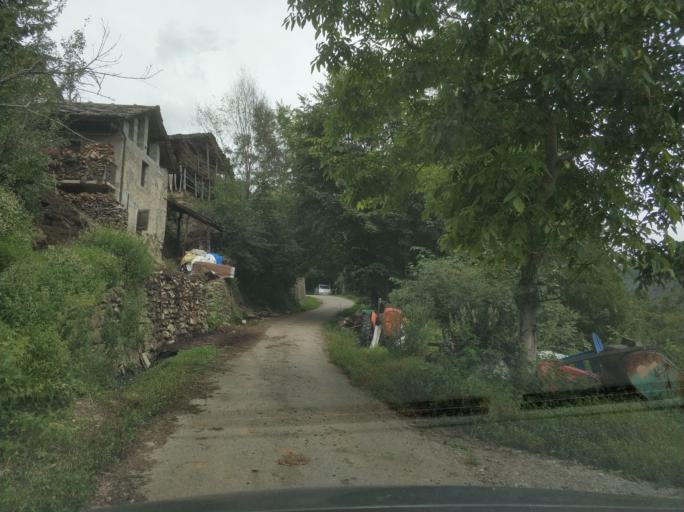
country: IT
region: Piedmont
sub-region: Provincia di Torino
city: Viu
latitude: 45.2153
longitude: 7.3933
